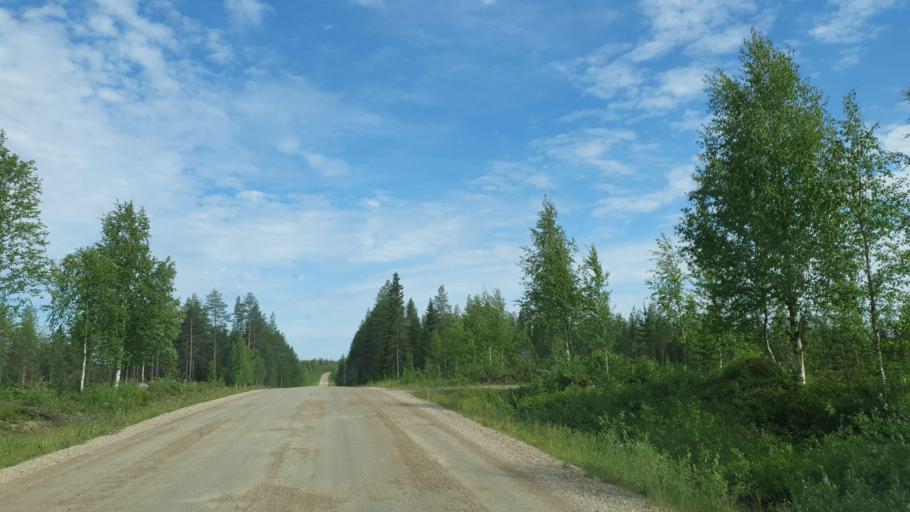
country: FI
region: Kainuu
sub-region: Kehys-Kainuu
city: Kuhmo
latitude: 64.4907
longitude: 29.4979
